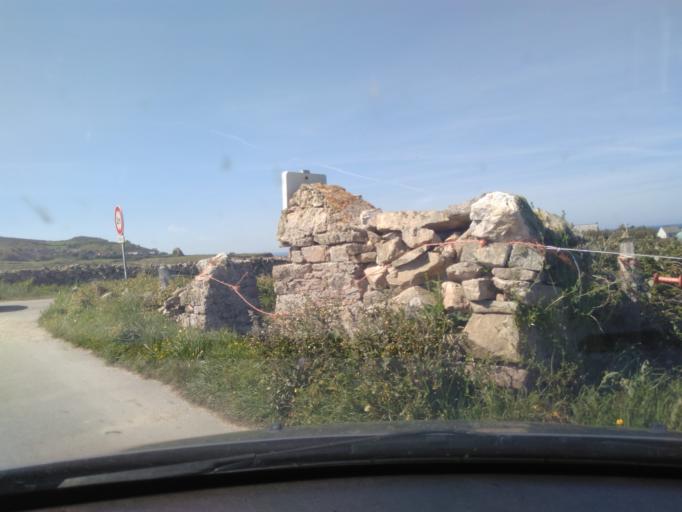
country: FR
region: Lower Normandy
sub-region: Departement de la Manche
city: Beaumont-Hague
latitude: 49.7161
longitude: -1.9414
